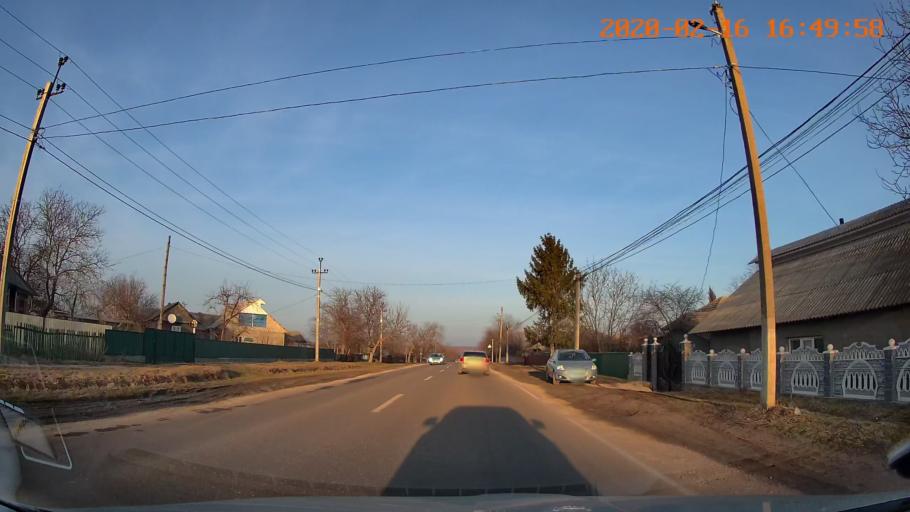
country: RO
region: Botosani
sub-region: Comuna Radauti-Prut
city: Miorcani
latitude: 48.2933
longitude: 26.9262
